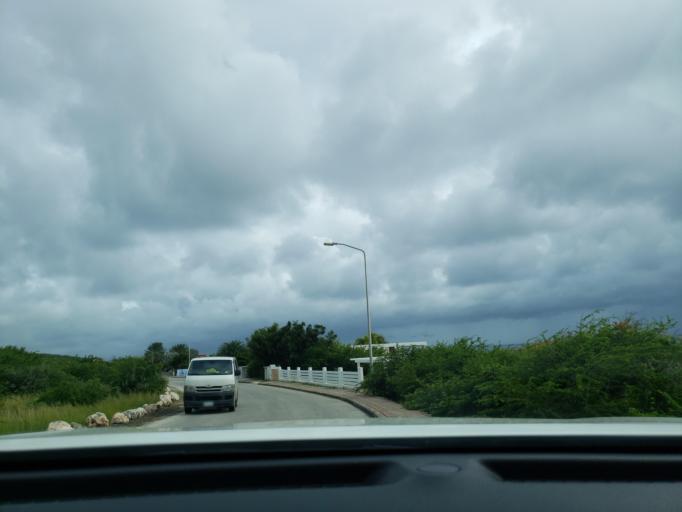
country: CW
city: Dorp Soto
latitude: 12.1969
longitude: -69.0755
